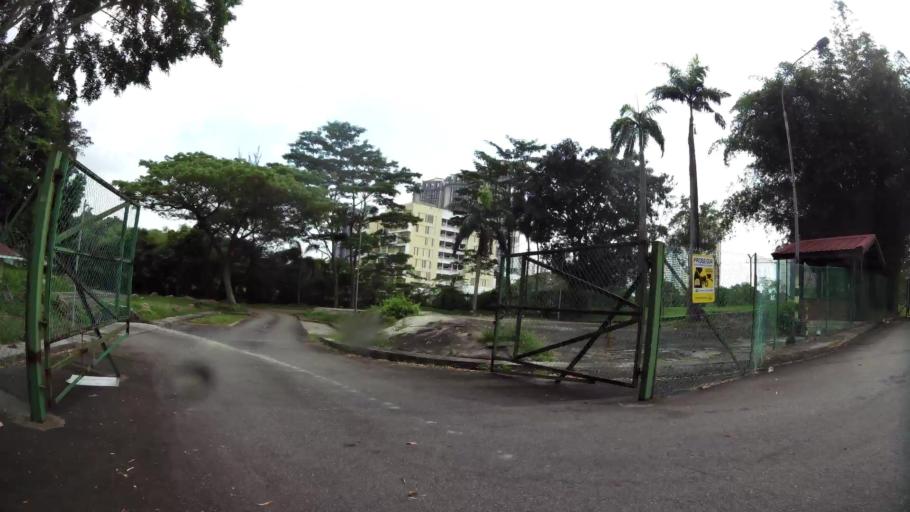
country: SG
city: Singapore
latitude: 1.2992
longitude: 103.8070
